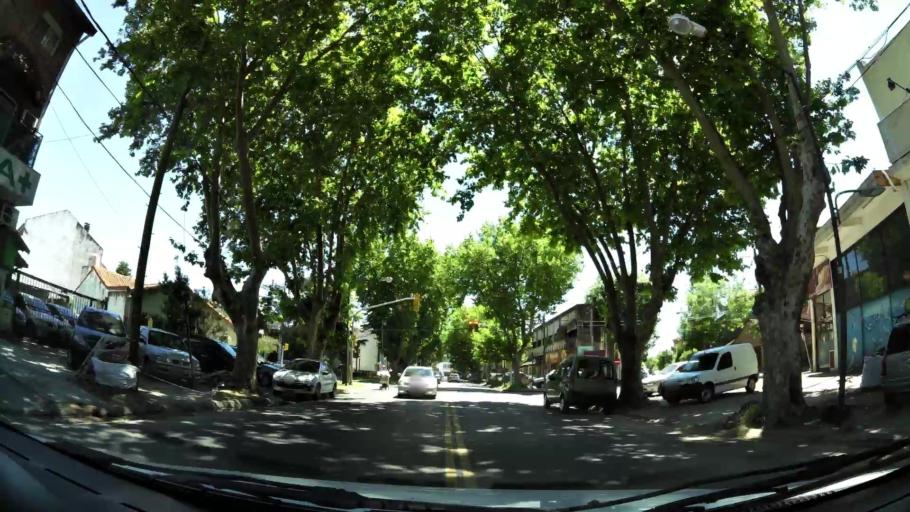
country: AR
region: Buenos Aires
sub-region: Partido de San Isidro
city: San Isidro
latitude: -34.5110
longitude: -58.5405
